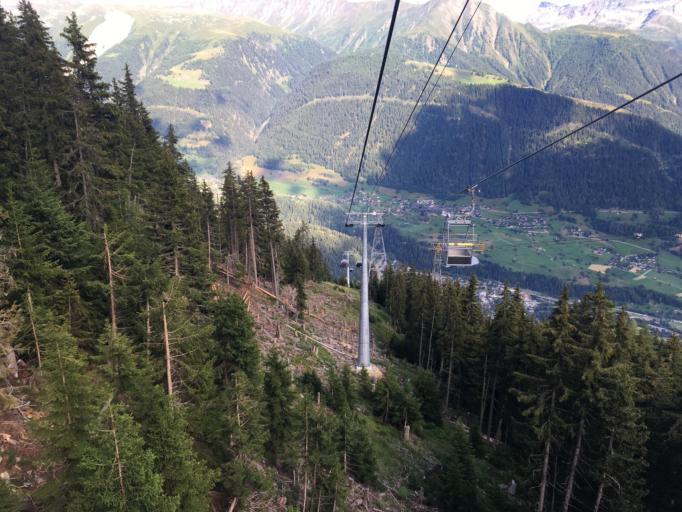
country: CH
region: Valais
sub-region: Goms District
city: Fiesch
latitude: 46.4114
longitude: 8.1115
